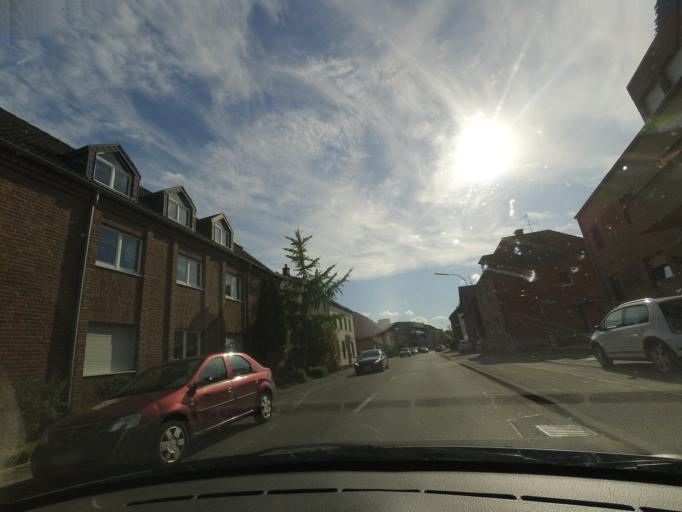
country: DE
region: North Rhine-Westphalia
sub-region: Regierungsbezirk Dusseldorf
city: Korschenbroich
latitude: 51.1910
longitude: 6.5567
